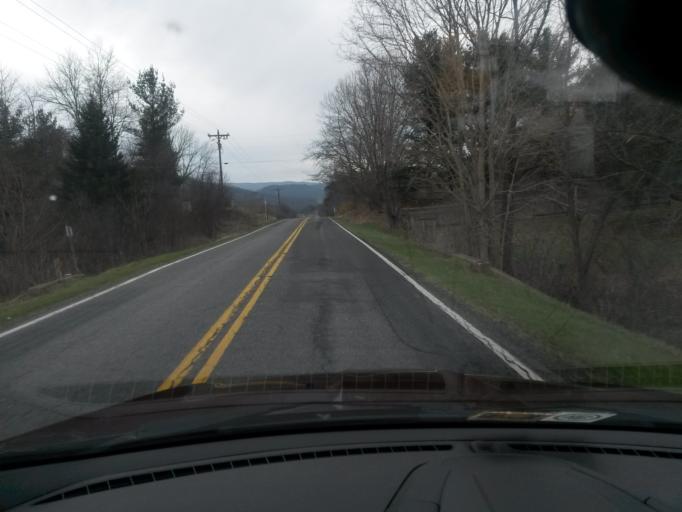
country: US
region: Virginia
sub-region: Highland County
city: Monterey
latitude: 38.2651
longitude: -79.6737
